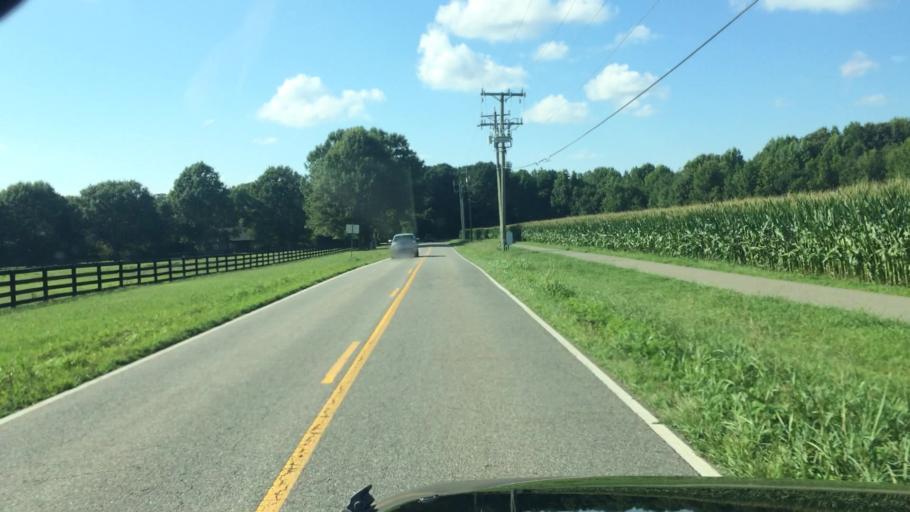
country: US
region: Virginia
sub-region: James City County
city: Williamsburg
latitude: 37.2356
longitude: -76.7855
